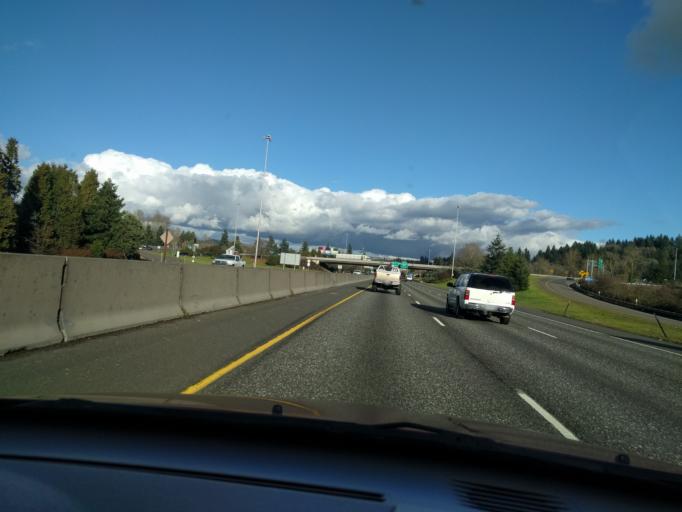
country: US
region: Oregon
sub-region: Clackamas County
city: Gladstone
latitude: 45.3731
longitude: -122.5898
